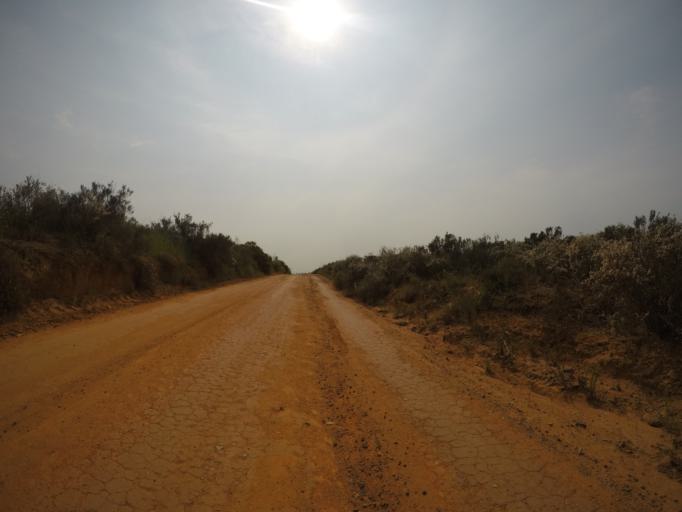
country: ZA
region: Western Cape
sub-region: West Coast District Municipality
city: Malmesbury
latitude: -33.4481
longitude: 18.7468
